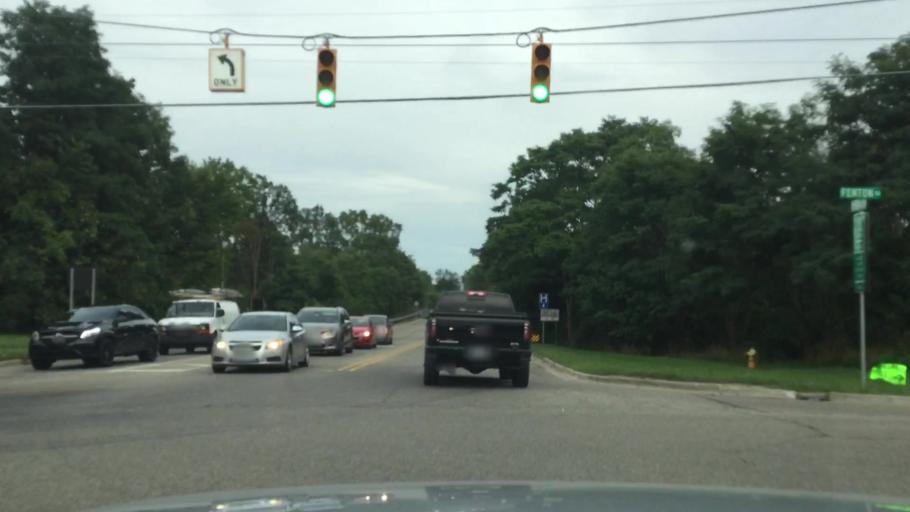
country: US
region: Michigan
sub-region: Genesee County
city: Lake Fenton
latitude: 42.8857
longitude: -83.6972
